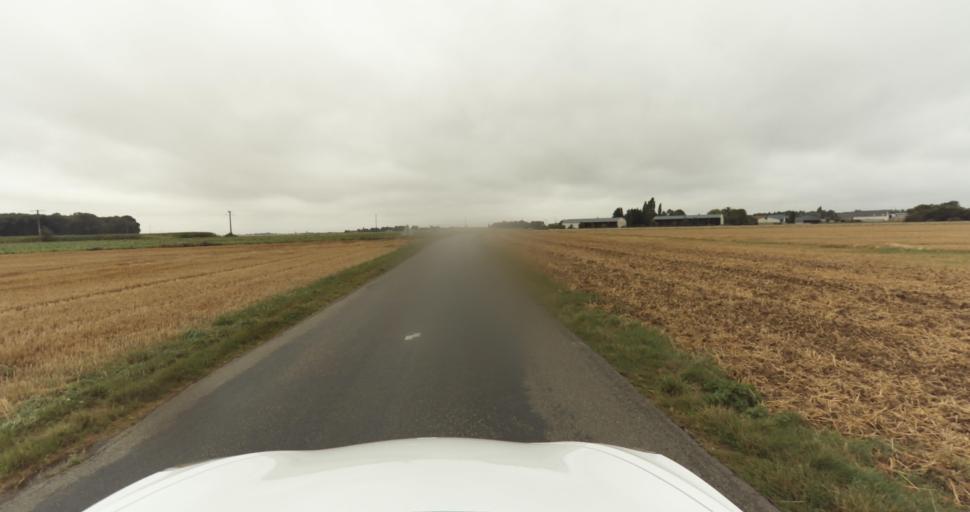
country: FR
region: Haute-Normandie
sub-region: Departement de l'Eure
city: Aviron
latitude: 49.0652
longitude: 1.1206
